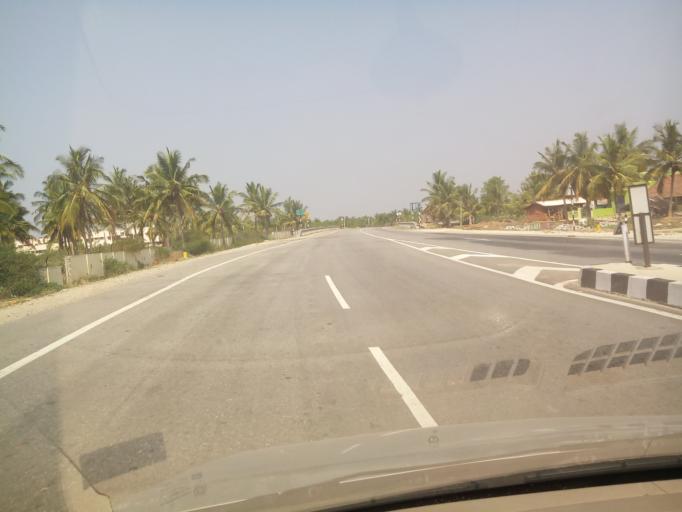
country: IN
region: Karnataka
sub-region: Hassan
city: Channarayapatna
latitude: 12.9074
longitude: 76.4247
